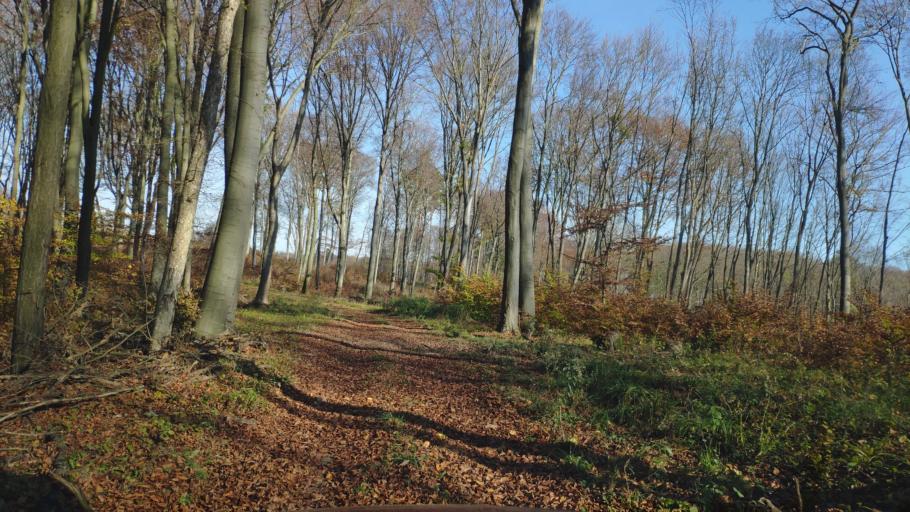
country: SK
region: Presovsky
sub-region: Okres Presov
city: Presov
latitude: 48.8958
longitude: 21.2103
